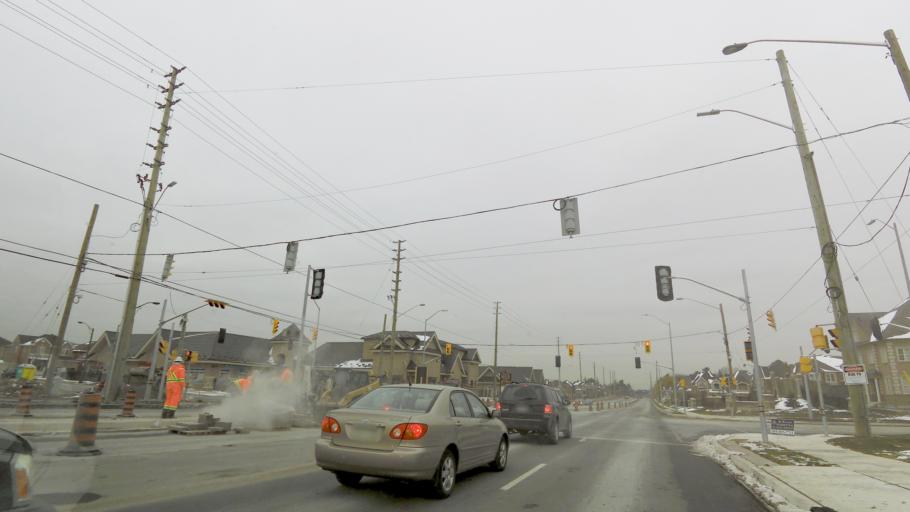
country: CA
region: Ontario
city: Vaughan
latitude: 43.8429
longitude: -79.5711
